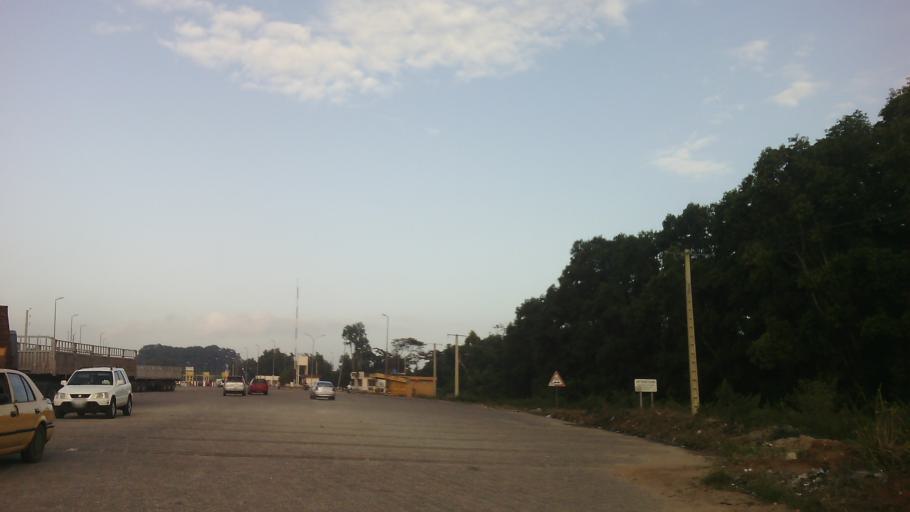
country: BJ
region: Atlantique
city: Ouidah
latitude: 6.3738
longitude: 2.1460
